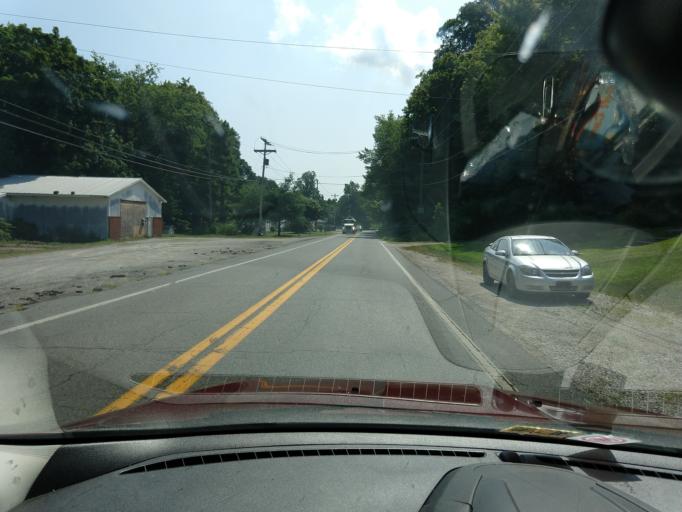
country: US
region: West Virginia
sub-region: Mason County
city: New Haven
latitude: 38.9850
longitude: -81.9617
